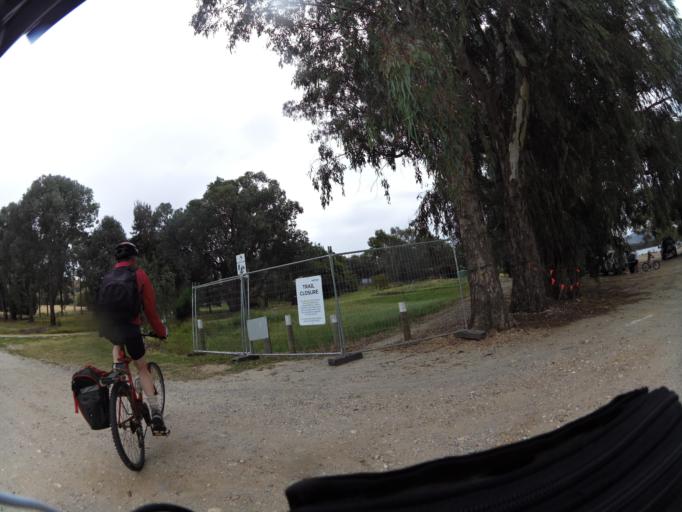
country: AU
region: New South Wales
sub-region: Albury Municipality
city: East Albury
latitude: -36.2198
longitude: 147.0682
